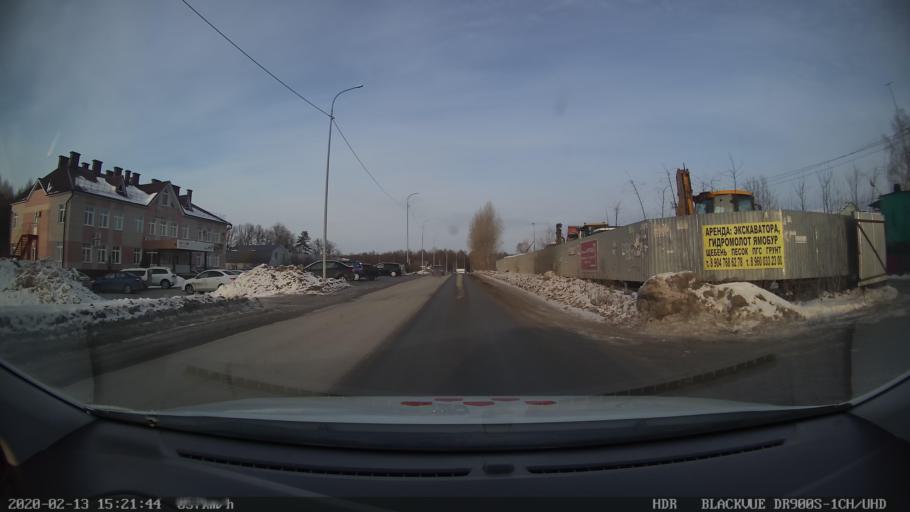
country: RU
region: Tatarstan
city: Vysokaya Gora
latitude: 55.9199
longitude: 49.3026
